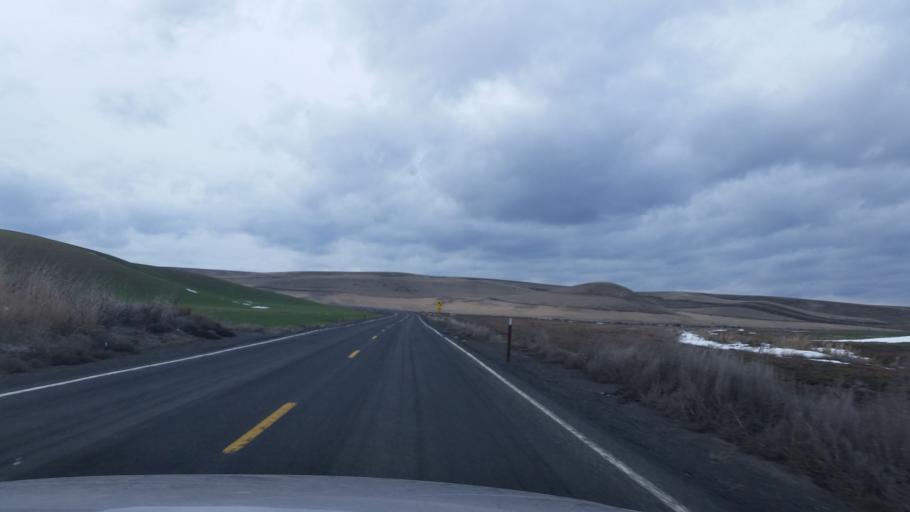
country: US
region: Washington
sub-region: Spokane County
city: Cheney
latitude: 47.1523
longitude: -117.8420
